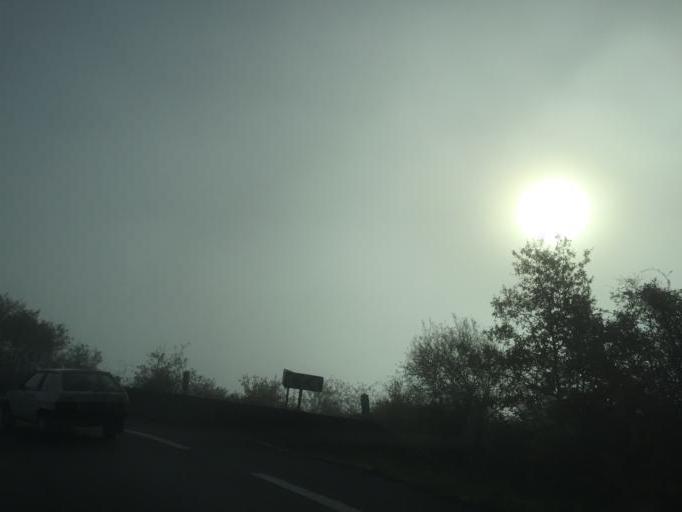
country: FR
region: Rhone-Alpes
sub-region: Departement du Rhone
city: Montagny
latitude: 45.6415
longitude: 4.7488
